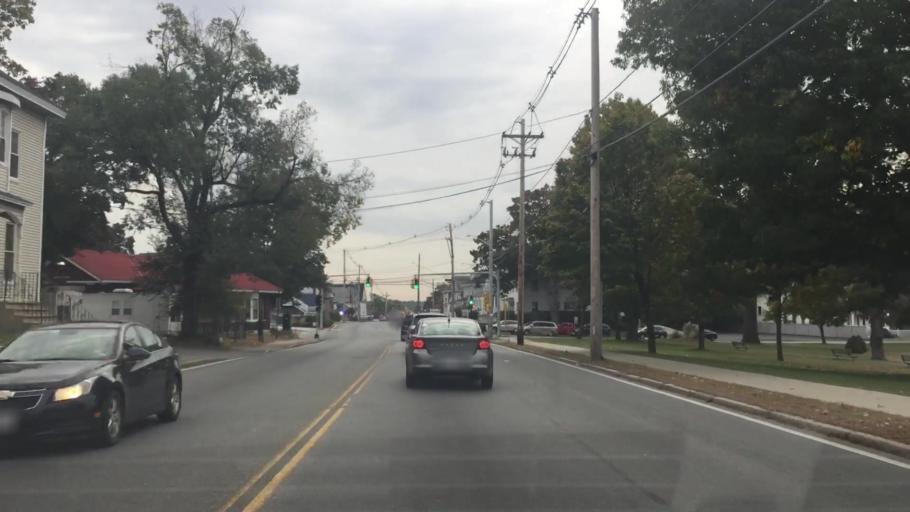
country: US
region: Massachusetts
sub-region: Middlesex County
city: Lowell
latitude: 42.6324
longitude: -71.2878
